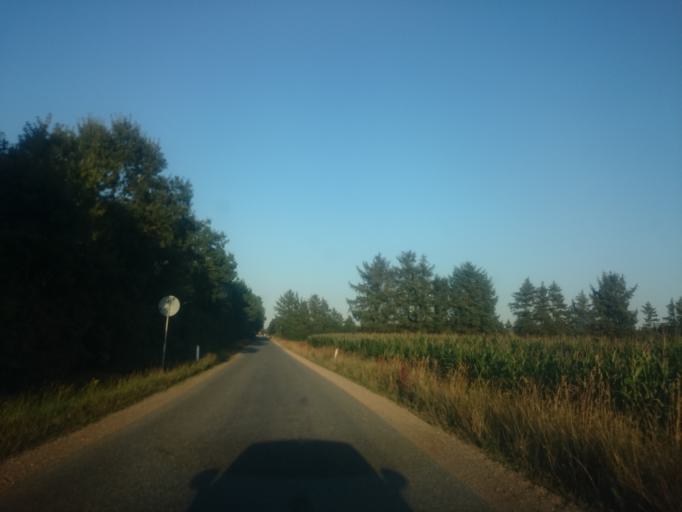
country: DK
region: South Denmark
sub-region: Billund Kommune
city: Billund
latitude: 55.7107
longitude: 9.0972
